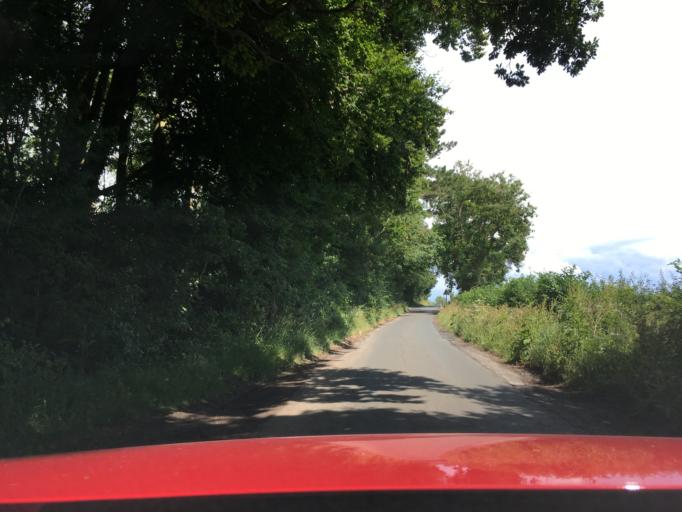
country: GB
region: England
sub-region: Gloucestershire
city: Chalford
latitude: 51.6956
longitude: -2.1247
